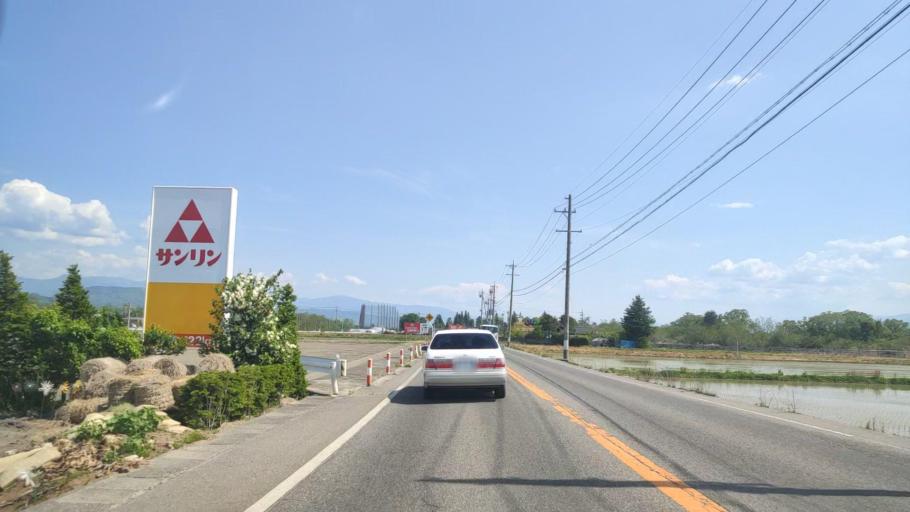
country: JP
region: Nagano
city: Hotaka
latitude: 36.3866
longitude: 137.8653
